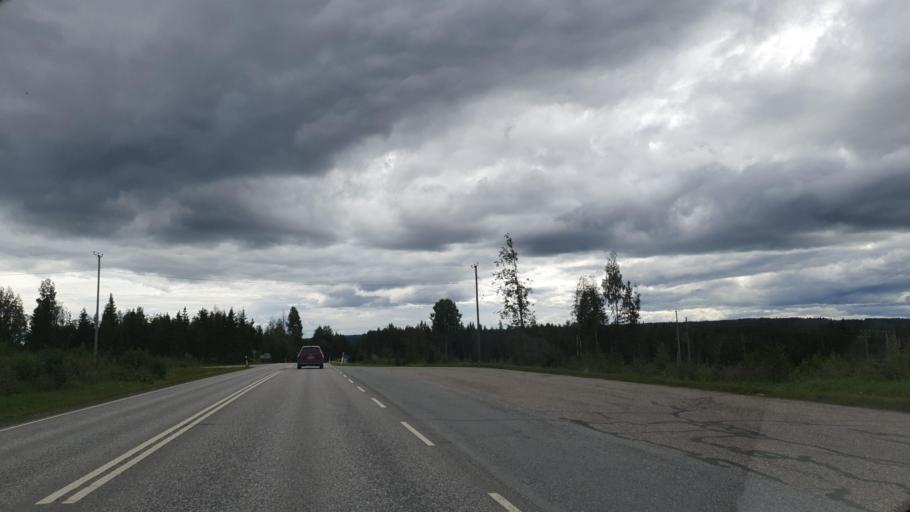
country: FI
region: Northern Savo
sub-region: Ylae-Savo
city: Sonkajaervi
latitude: 63.7451
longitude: 27.3831
